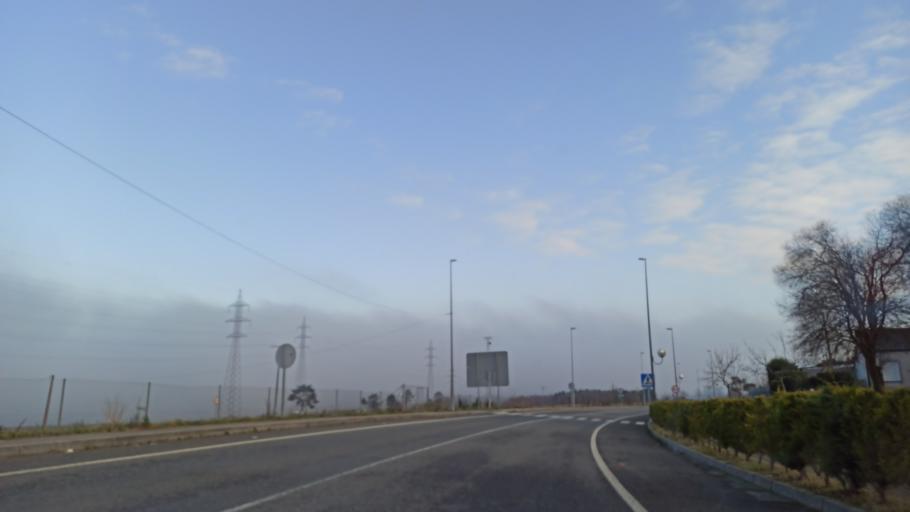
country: ES
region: Galicia
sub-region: Provincia da Coruna
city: As Pontes de Garcia Rodriguez
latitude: 43.4533
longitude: -7.8675
